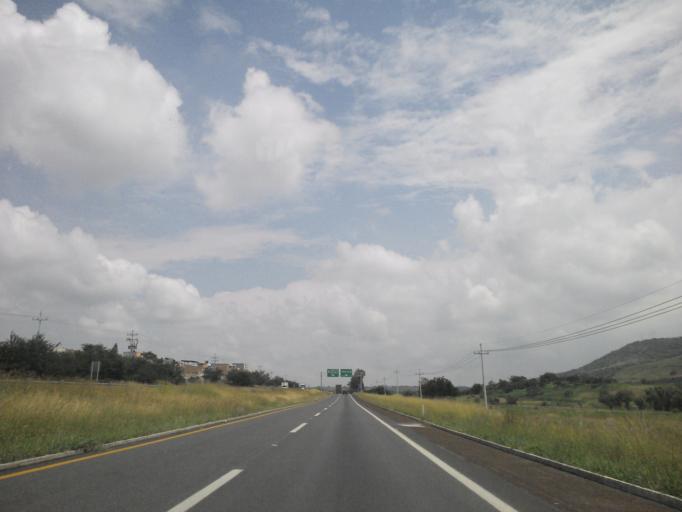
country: MX
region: Jalisco
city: Zapotlanejo
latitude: 20.6176
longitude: -103.0659
